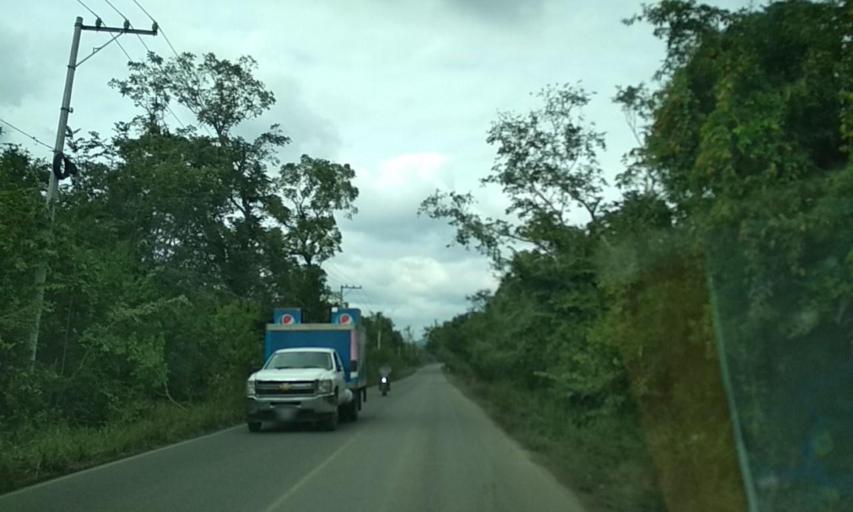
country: MX
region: Veracruz
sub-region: Papantla
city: El Chote
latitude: 20.3786
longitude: -97.3357
